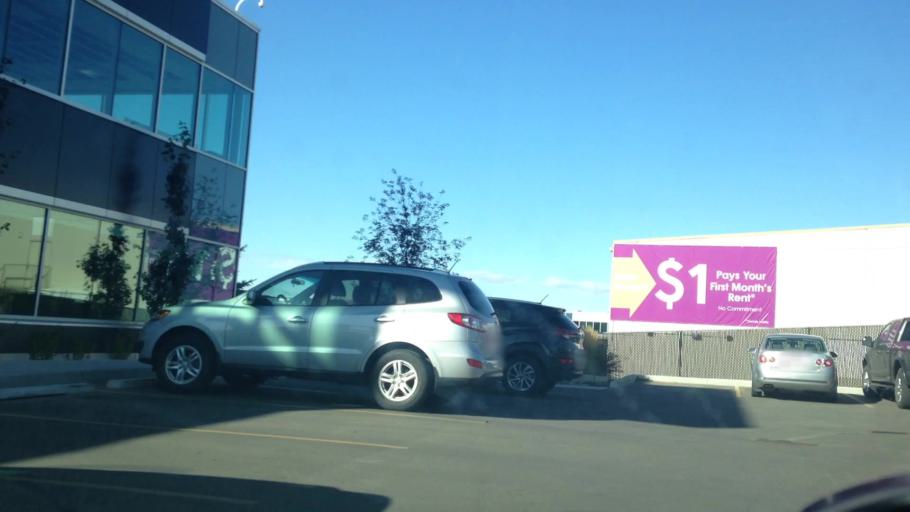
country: CA
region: Alberta
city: Calgary
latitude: 51.1418
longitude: -114.0728
